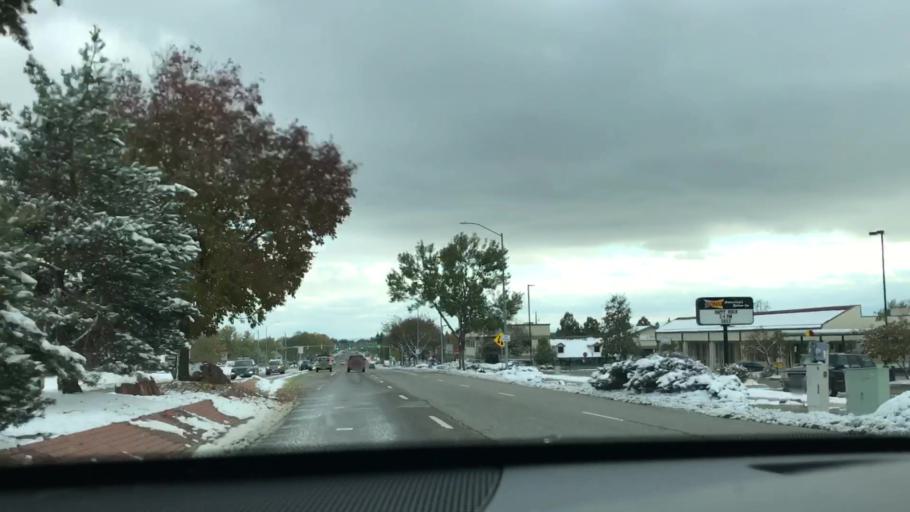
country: US
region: Colorado
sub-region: Boulder County
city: Longmont
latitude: 40.2018
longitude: -105.1026
